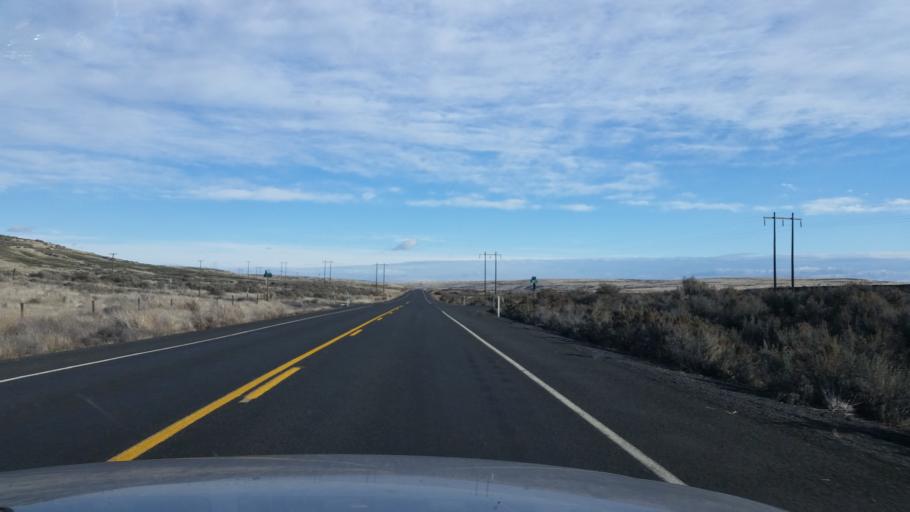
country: US
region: Washington
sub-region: Adams County
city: Ritzville
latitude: 47.3477
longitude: -118.5949
